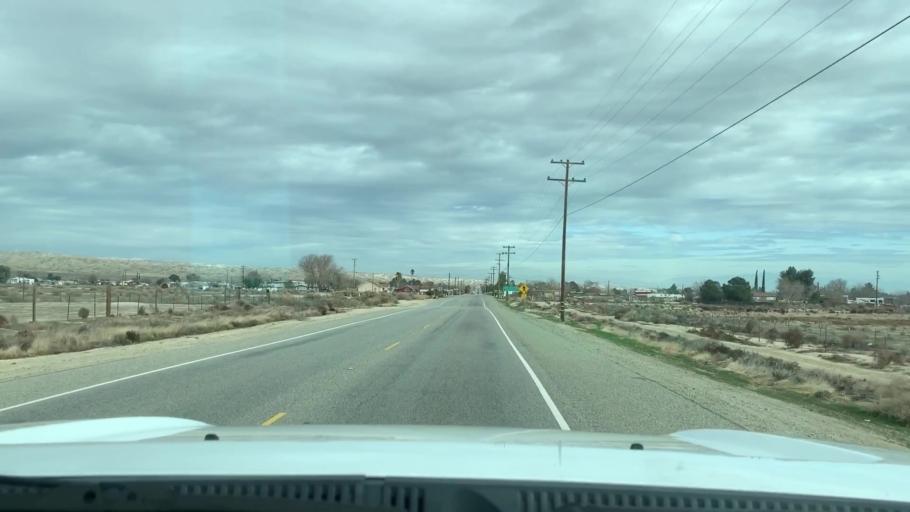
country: US
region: California
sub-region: Kern County
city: Ford City
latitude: 35.2158
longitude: -119.3959
